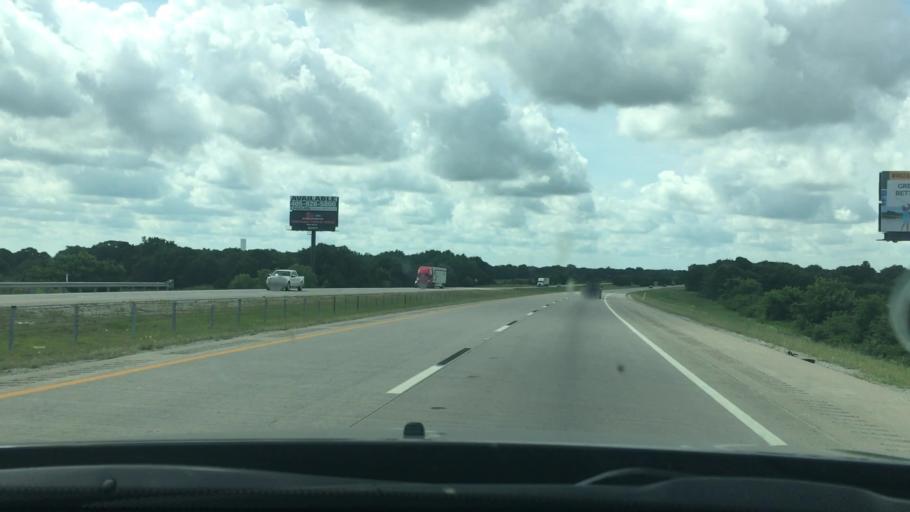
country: US
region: Oklahoma
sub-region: Love County
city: Marietta
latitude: 33.8337
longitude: -97.1314
